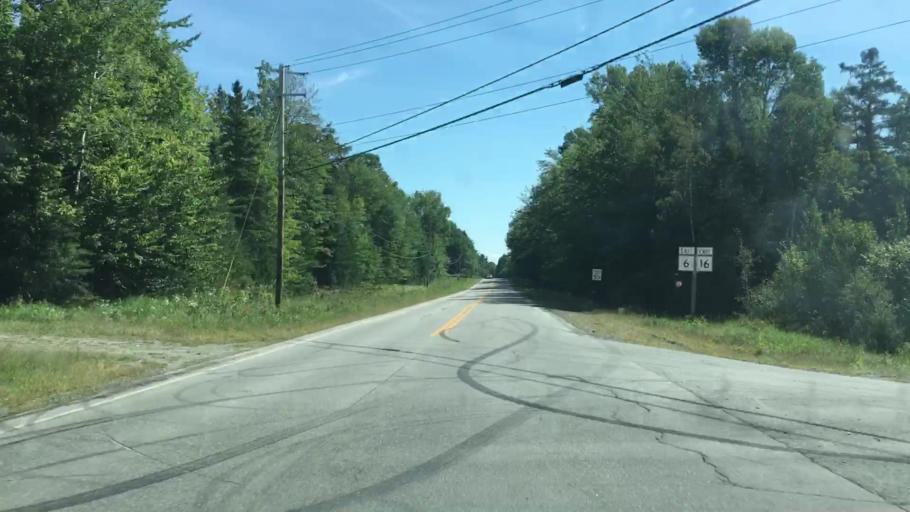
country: US
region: Maine
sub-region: Piscataquis County
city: Milo
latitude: 45.1992
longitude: -68.9057
